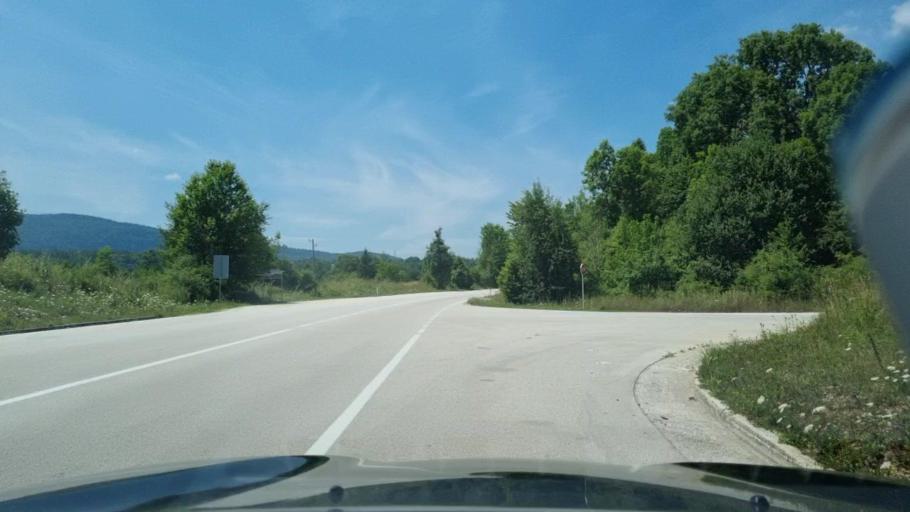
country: BA
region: Federation of Bosnia and Herzegovina
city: Sanica
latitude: 44.5489
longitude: 16.5783
